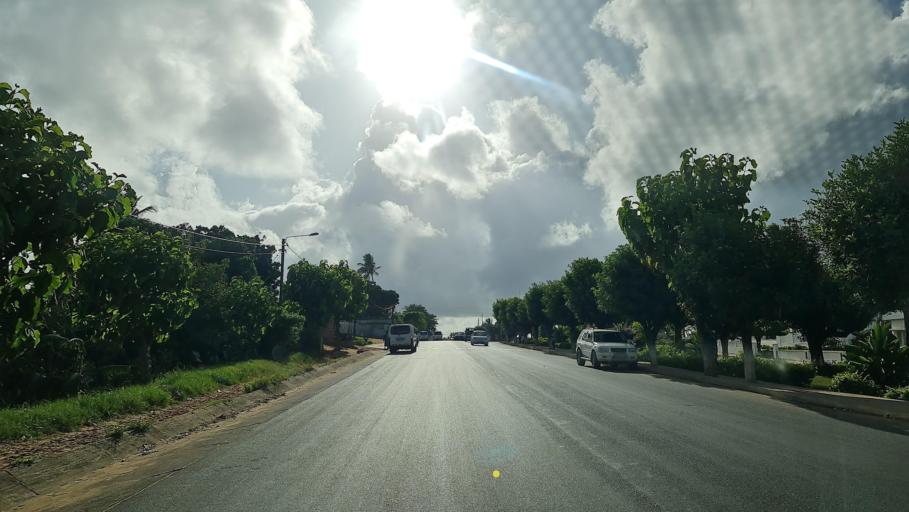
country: MZ
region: Gaza
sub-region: Xai-Xai District
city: Xai-Xai
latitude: -25.0568
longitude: 33.6545
